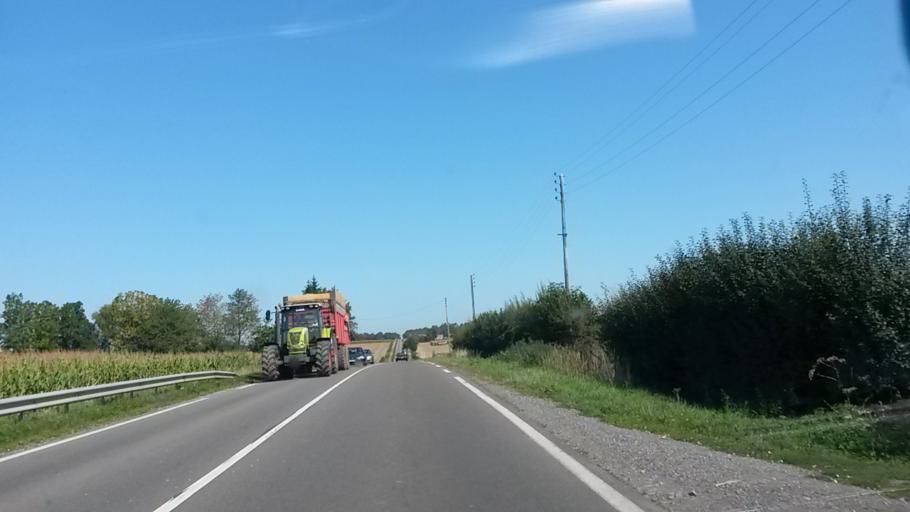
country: FR
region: Nord-Pas-de-Calais
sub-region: Departement du Nord
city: Avesnelles
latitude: 50.1794
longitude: 3.9525
